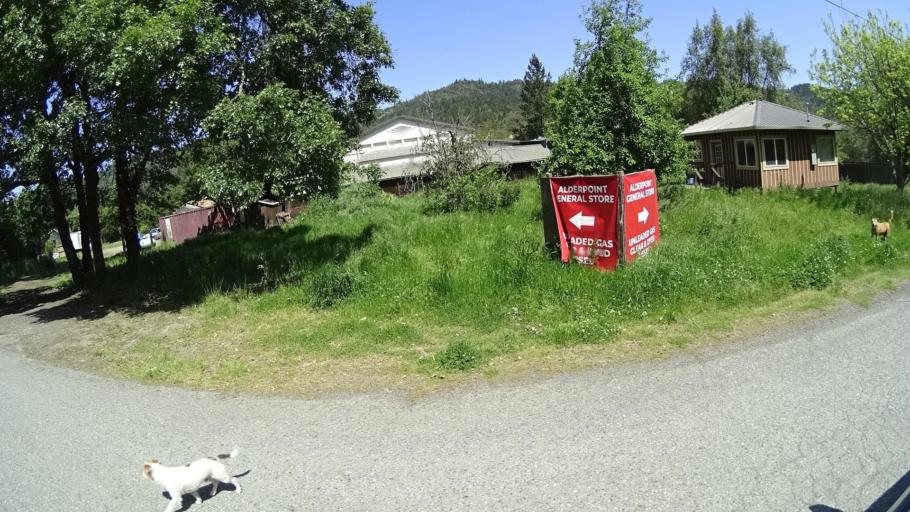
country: US
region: California
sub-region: Humboldt County
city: Redway
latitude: 40.1756
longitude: -123.6090
